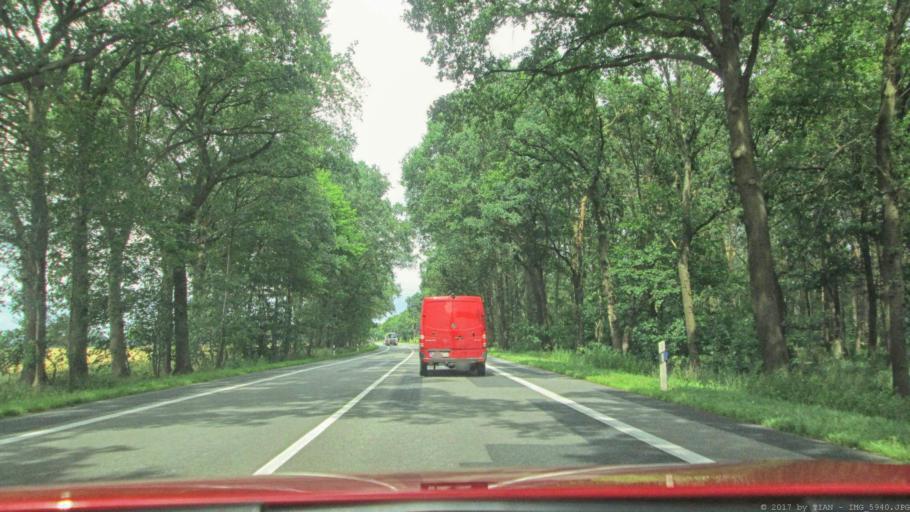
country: DE
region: Lower Saxony
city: Jelmstorf
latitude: 53.1232
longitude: 10.5069
